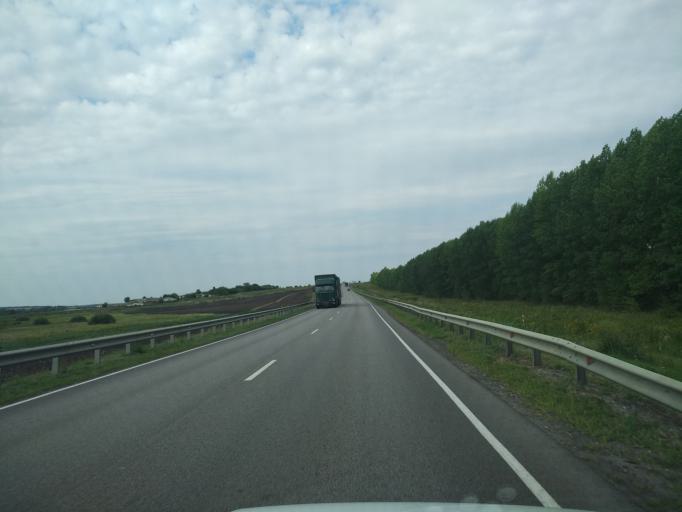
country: RU
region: Voronezj
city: Pereleshinskiy
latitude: 51.8560
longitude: 40.3383
